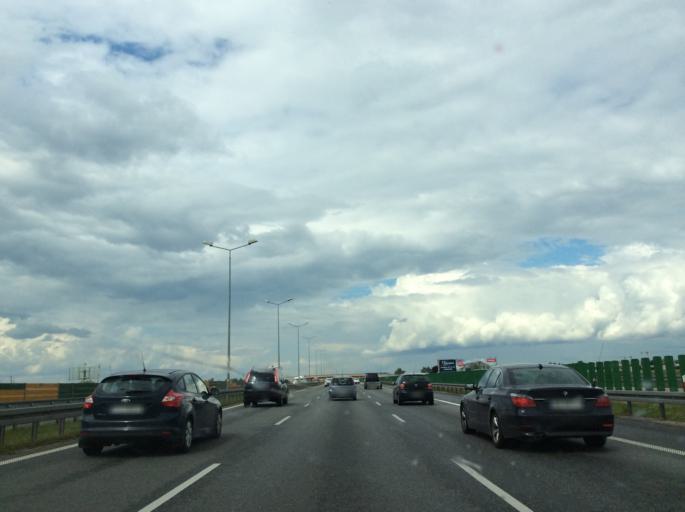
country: PL
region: Masovian Voivodeship
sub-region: Warszawa
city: Ursus
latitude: 52.2239
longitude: 20.8723
